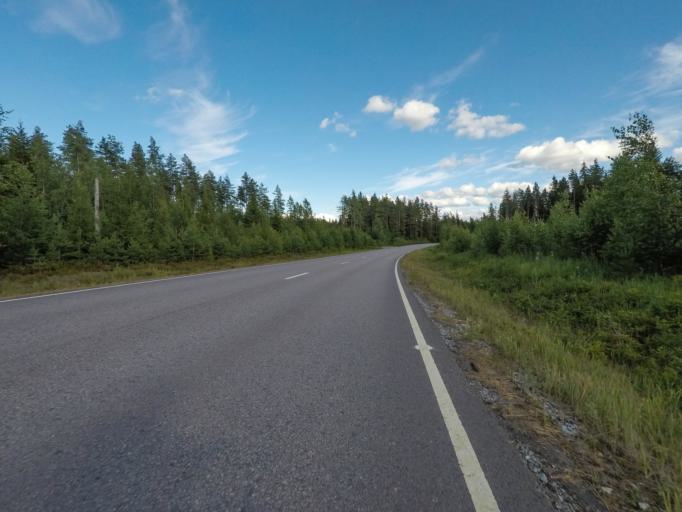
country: FI
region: South Karelia
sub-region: Lappeenranta
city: Joutseno
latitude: 61.1461
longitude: 28.6231
